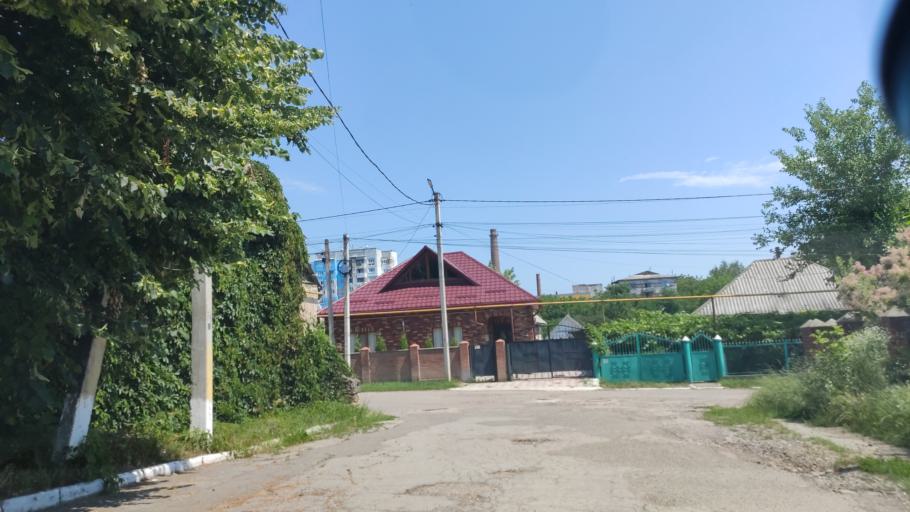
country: MD
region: Raionul Soroca
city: Soroca
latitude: 48.1670
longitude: 28.3086
